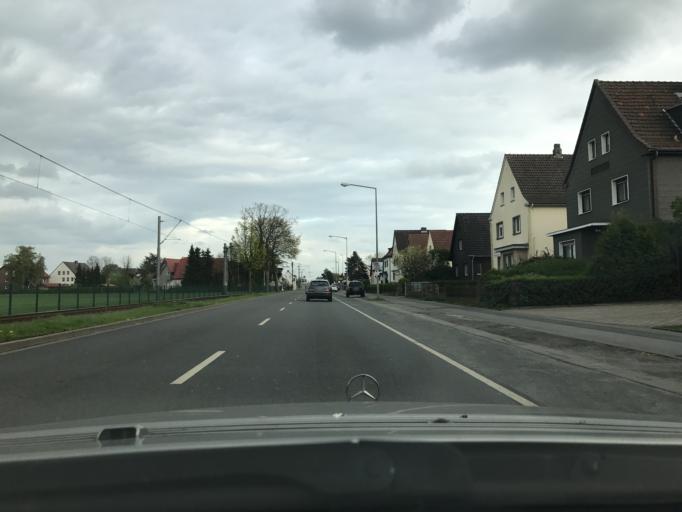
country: DE
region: North Rhine-Westphalia
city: Waltrop
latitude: 51.5835
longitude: 7.4523
